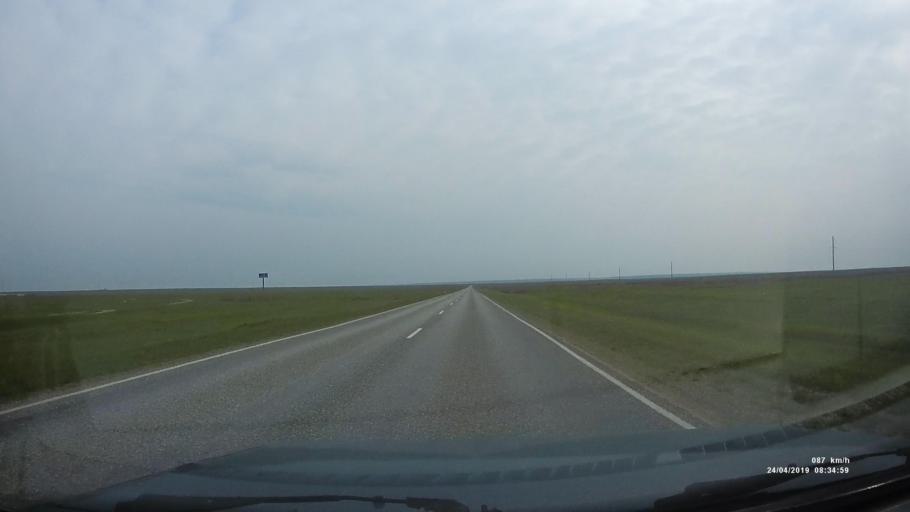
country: RU
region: Kalmykiya
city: Arshan'
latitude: 46.1942
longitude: 43.9124
